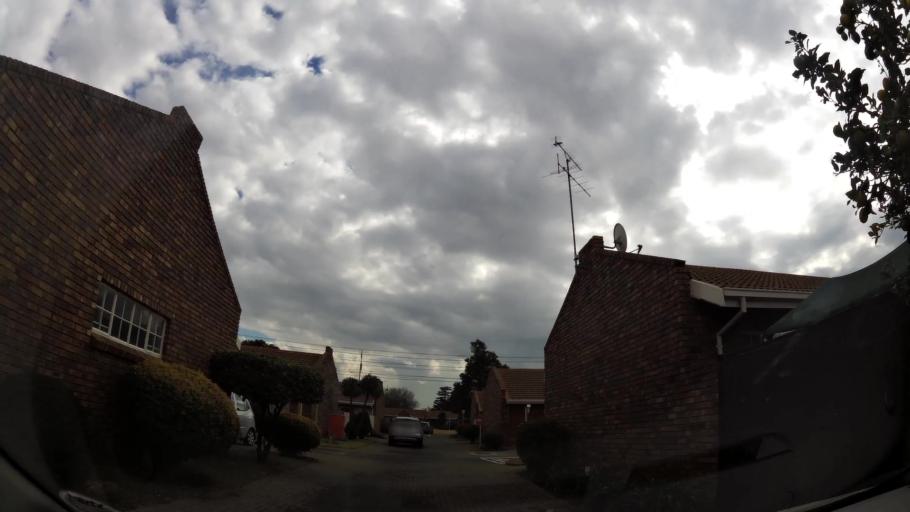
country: ZA
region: Gauteng
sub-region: Sedibeng District Municipality
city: Vereeniging
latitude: -26.6489
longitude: 27.9719
